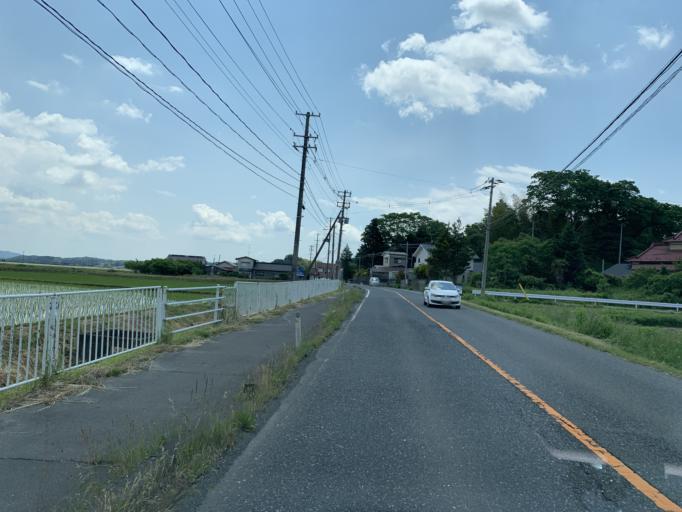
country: JP
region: Miyagi
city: Kogota
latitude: 38.5069
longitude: 141.0708
